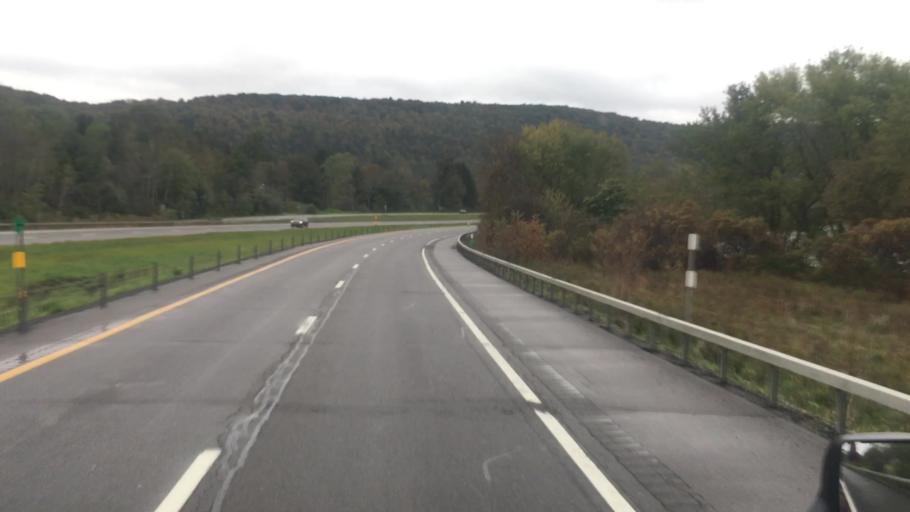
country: US
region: New York
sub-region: Tioga County
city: Apalachin
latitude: 42.0809
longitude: -76.2049
